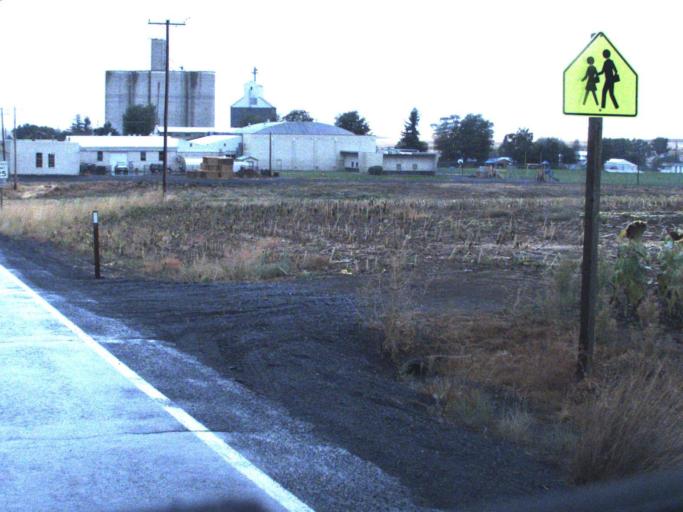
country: US
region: Washington
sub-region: Lincoln County
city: Davenport
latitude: 47.4784
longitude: -118.2484
